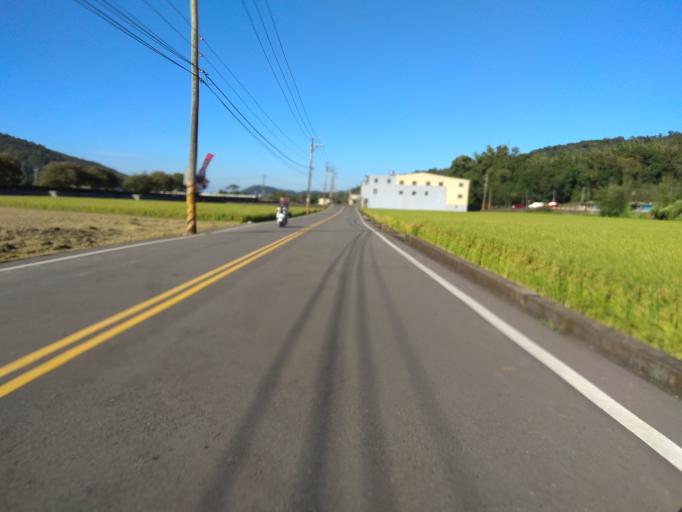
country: TW
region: Taiwan
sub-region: Hsinchu
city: Zhubei
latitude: 24.8446
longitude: 121.1403
